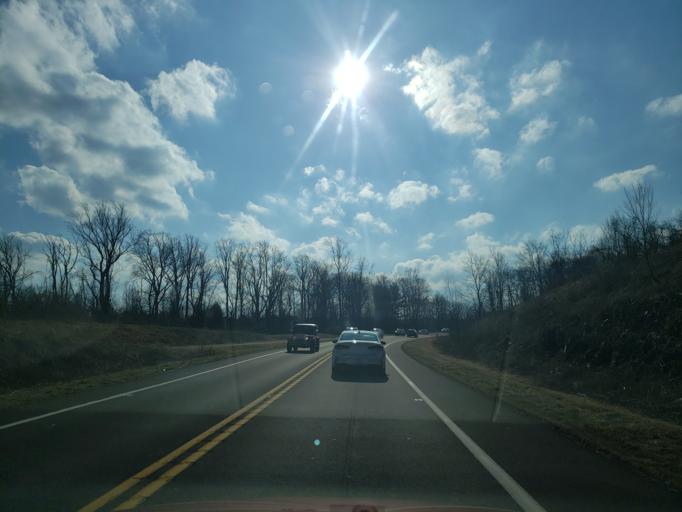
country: US
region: Pennsylvania
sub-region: Bucks County
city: Brittany Farms-Highlands
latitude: 40.2708
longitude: -75.1913
